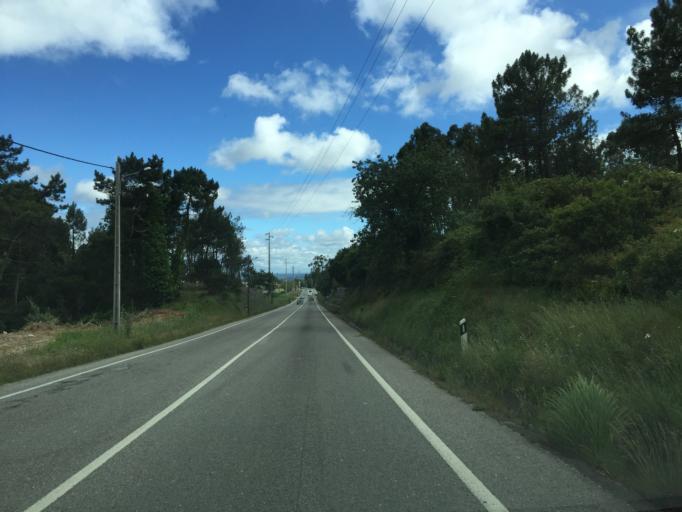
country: PT
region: Coimbra
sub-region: Figueira da Foz
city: Tavarede
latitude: 40.1841
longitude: -8.8293
